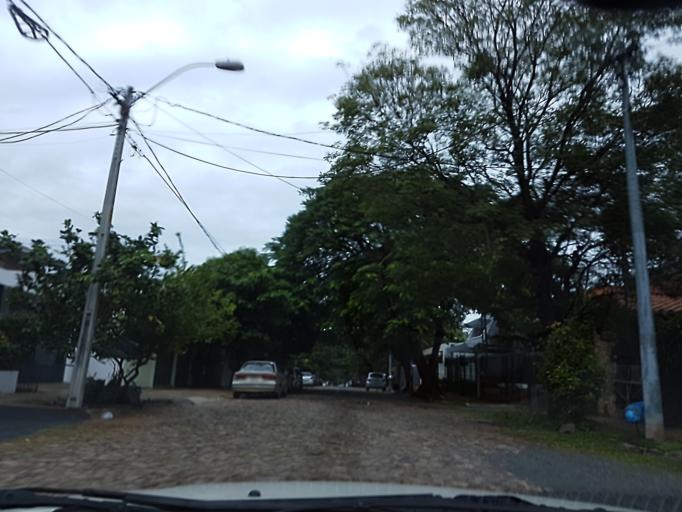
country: PY
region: Asuncion
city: Asuncion
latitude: -25.2839
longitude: -57.6001
